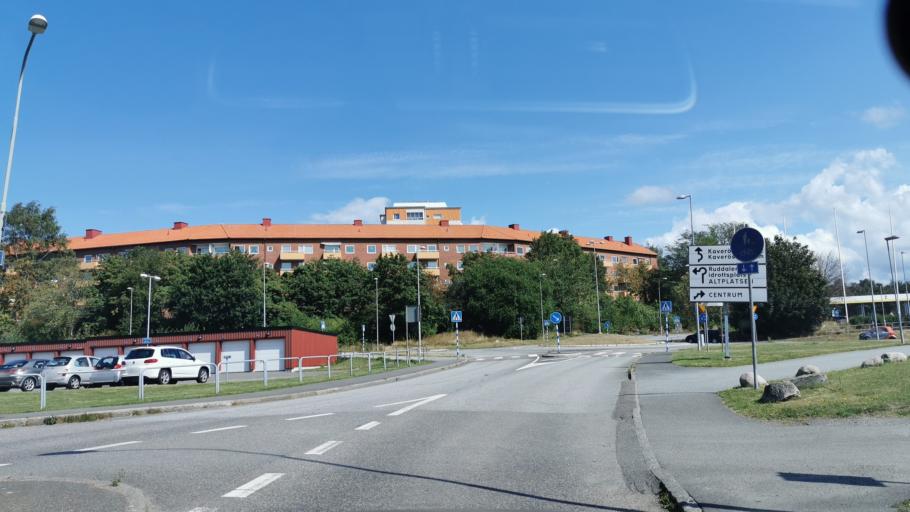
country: SE
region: Vaestra Goetaland
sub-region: Goteborg
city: Majorna
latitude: 57.6591
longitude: 11.9195
